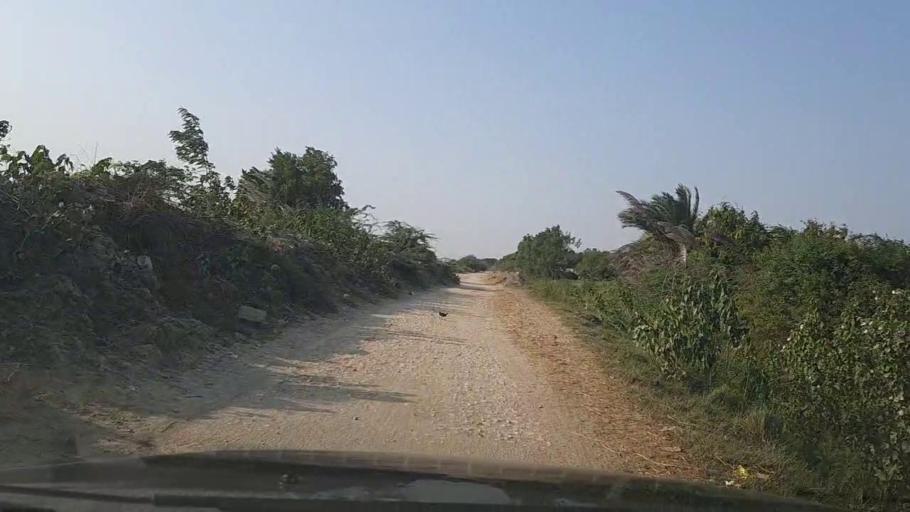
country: PK
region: Sindh
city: Mirpur Sakro
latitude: 24.6361
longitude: 67.7519
